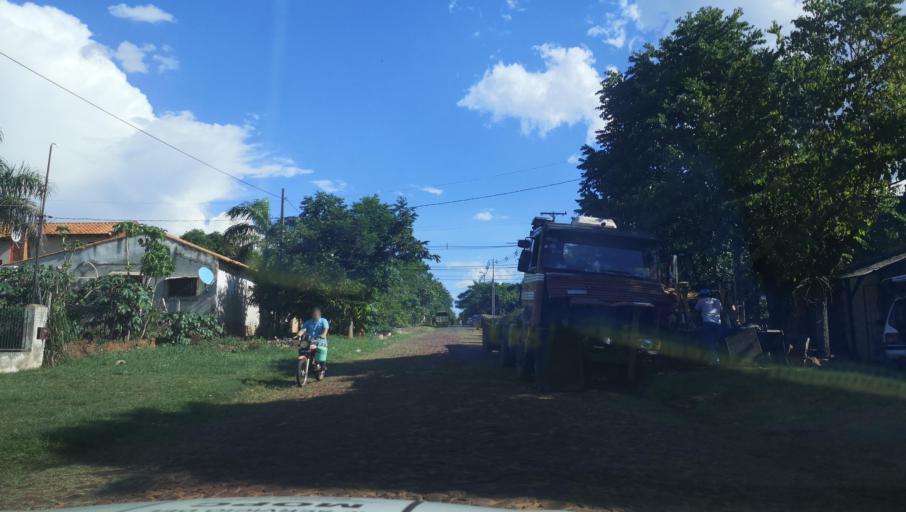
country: PY
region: Misiones
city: Santa Maria
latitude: -26.8844
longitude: -57.0195
